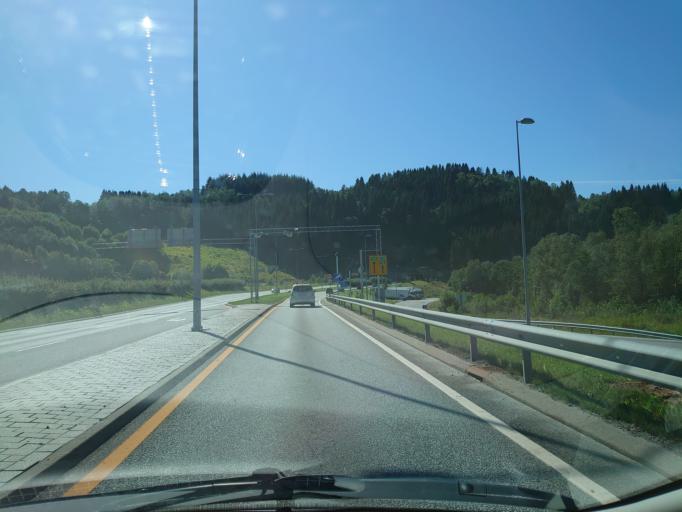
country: NO
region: Hordaland
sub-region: Bergen
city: Hylkje
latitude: 60.4818
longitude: 5.3714
